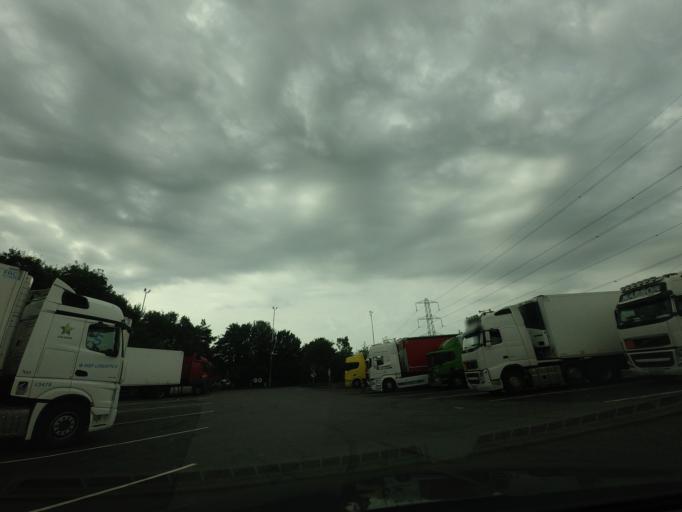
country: GB
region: England
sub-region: Central Bedfordshire
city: Harlington
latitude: 51.9484
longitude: -0.4994
